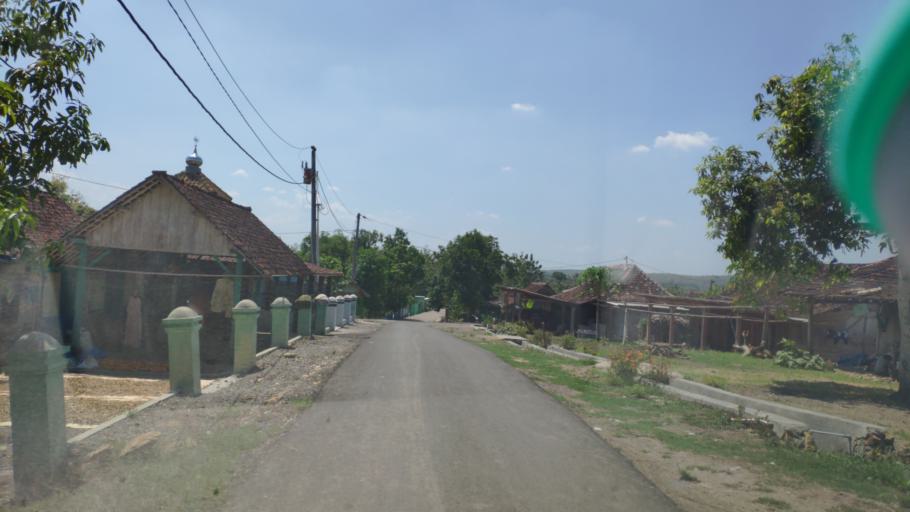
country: ID
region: Central Java
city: Galuk
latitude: -7.0914
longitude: 111.5031
